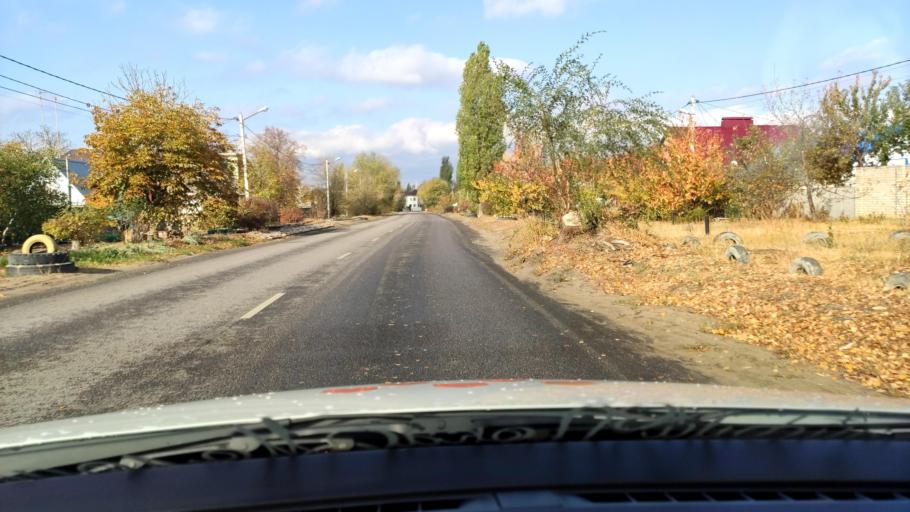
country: RU
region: Voronezj
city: Pridonskoy
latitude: 51.6818
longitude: 39.0735
